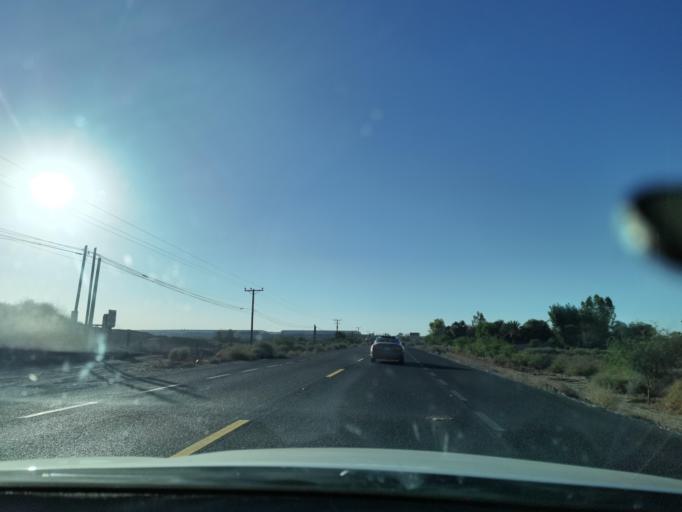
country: MX
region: Baja California
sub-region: Mexicali
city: Islas Agrarias Grupo A
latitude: 32.6388
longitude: -115.2933
